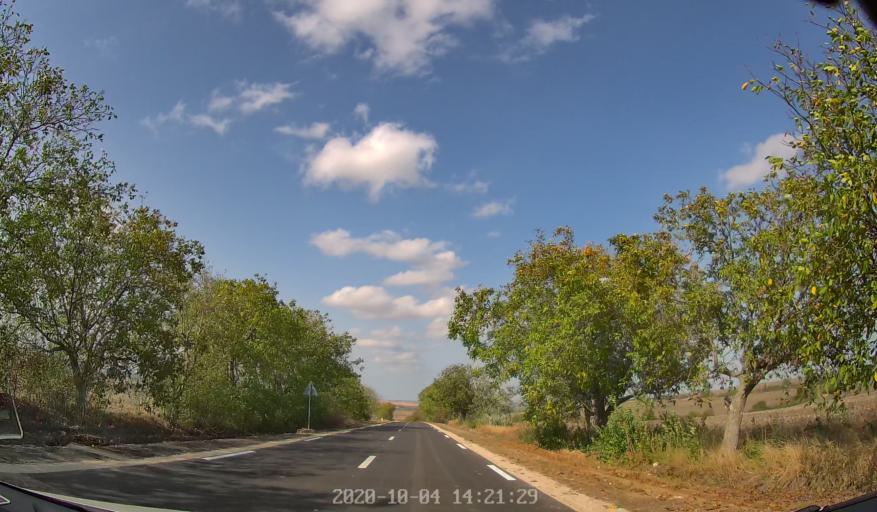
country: MD
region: Rezina
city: Saharna
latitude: 47.5856
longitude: 28.9553
